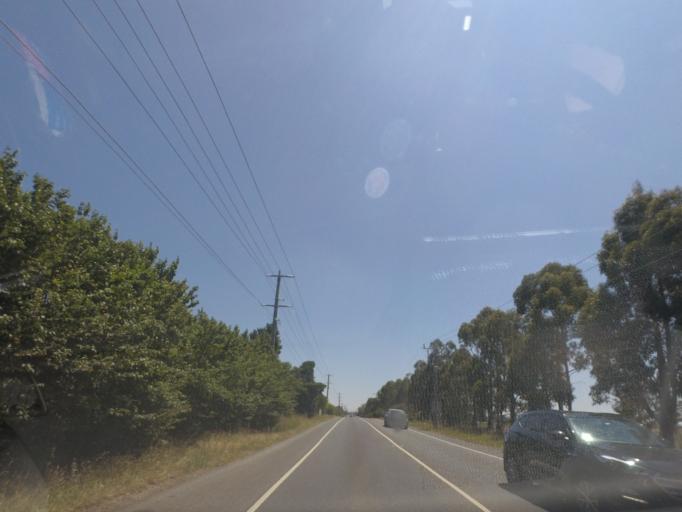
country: AU
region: Victoria
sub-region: Whittlesea
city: Epping
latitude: -37.6043
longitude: 145.0320
